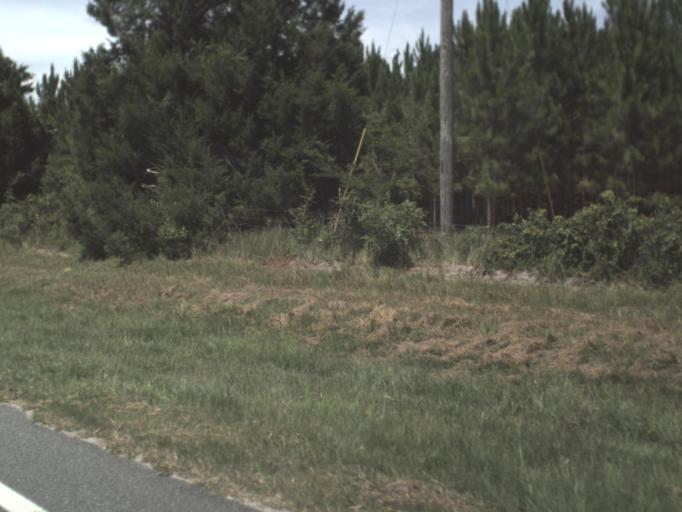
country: US
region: Florida
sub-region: Alachua County
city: High Springs
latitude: 29.9334
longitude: -82.8603
